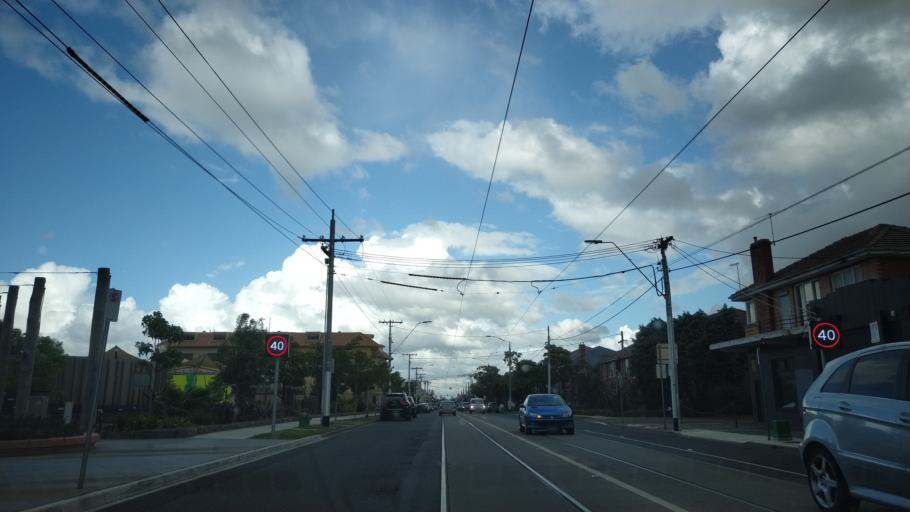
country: AU
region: Victoria
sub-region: Glen Eira
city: Glen Huntly
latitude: -37.8889
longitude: 145.0378
